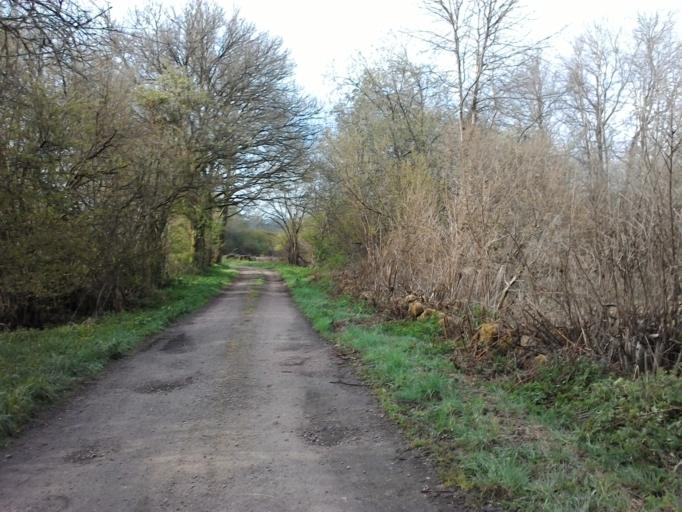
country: FR
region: Bourgogne
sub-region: Departement de la Cote-d'Or
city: Saulieu
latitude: 47.2515
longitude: 4.2087
